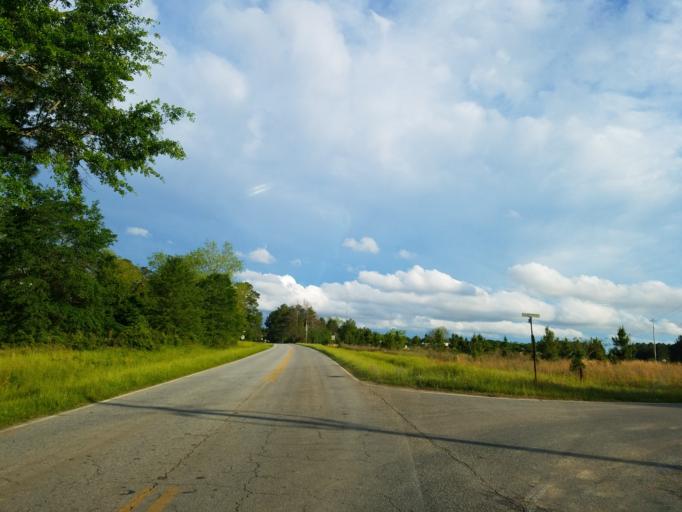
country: US
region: Georgia
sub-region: Crisp County
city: Cordele
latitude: 31.9376
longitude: -83.7854
